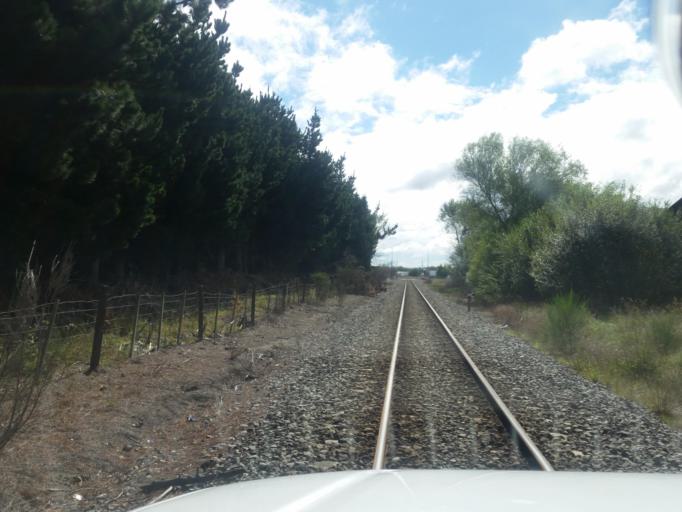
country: NZ
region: Canterbury
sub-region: Waimakariri District
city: Kaiapoi
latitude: -43.3940
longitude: 172.6562
